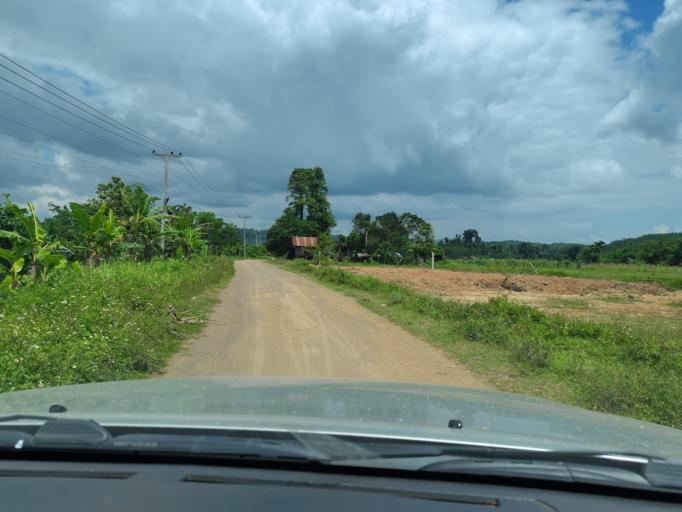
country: LA
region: Loungnamtha
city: Muang Long
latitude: 20.6822
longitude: 101.0511
